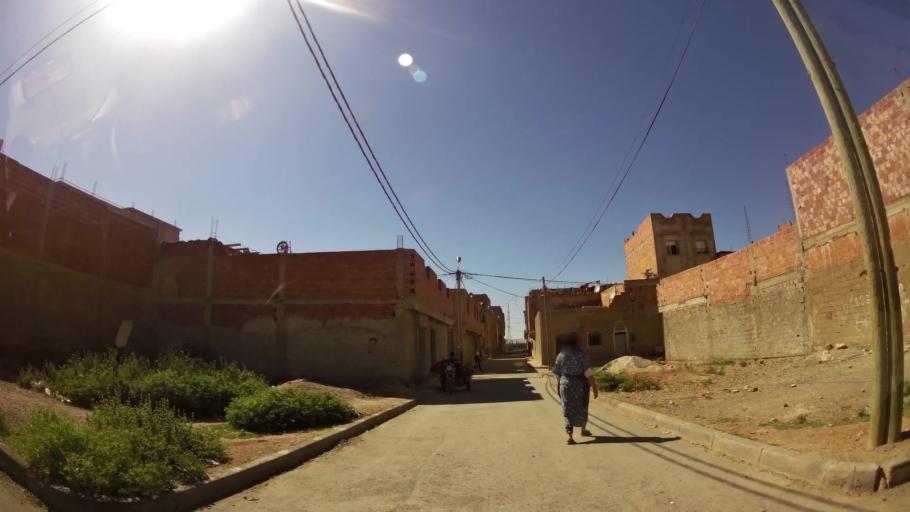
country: MA
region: Oriental
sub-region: Oujda-Angad
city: Oujda
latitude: 34.7212
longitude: -1.9040
